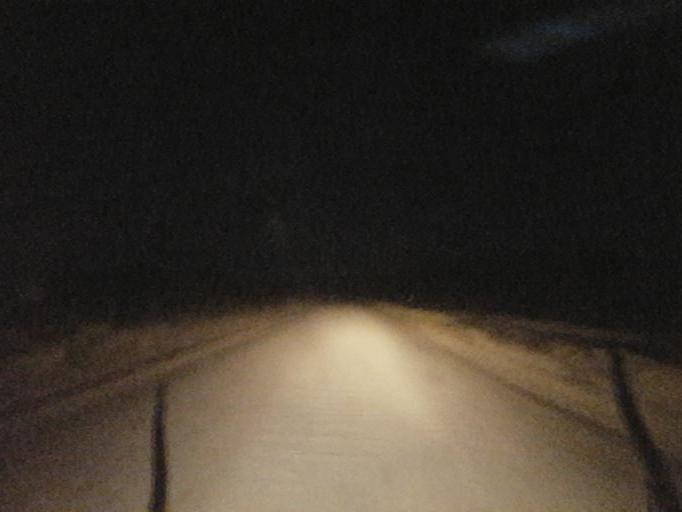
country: US
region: Colorado
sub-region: Rio Grande County
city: Monte Vista
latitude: 37.4011
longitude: -106.1158
